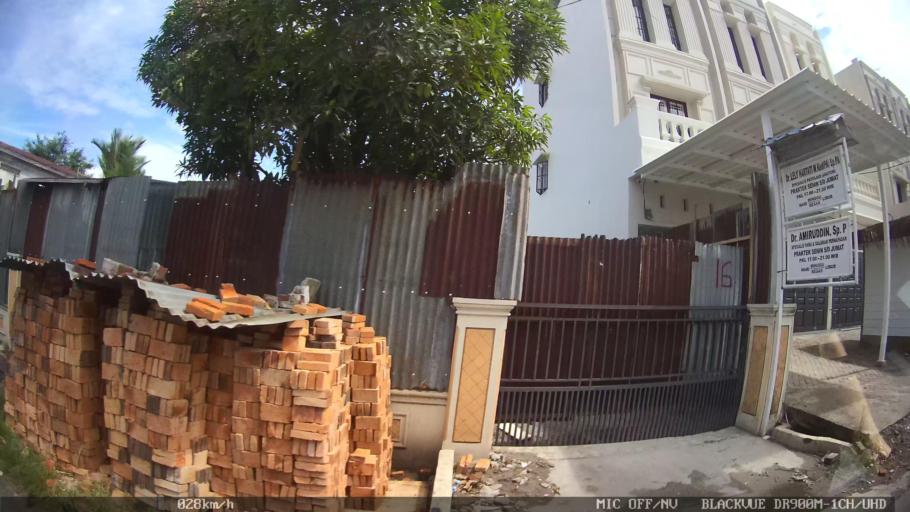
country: ID
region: North Sumatra
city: Medan
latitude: 3.5875
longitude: 98.7128
